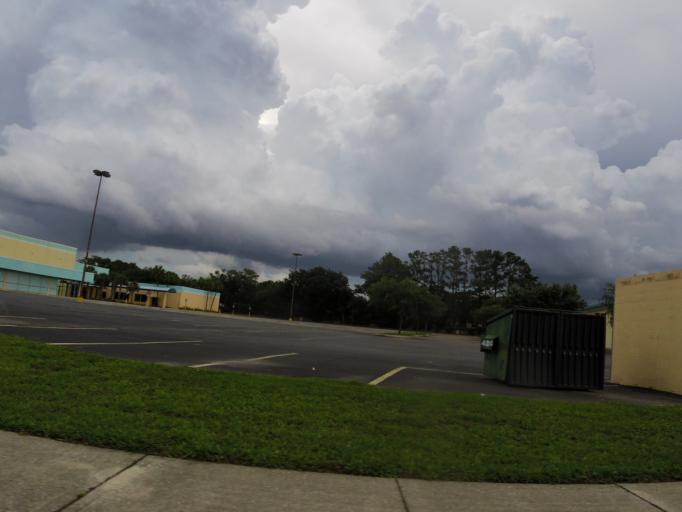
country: US
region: Florida
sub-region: Duval County
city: Jacksonville
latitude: 30.3697
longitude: -81.6678
